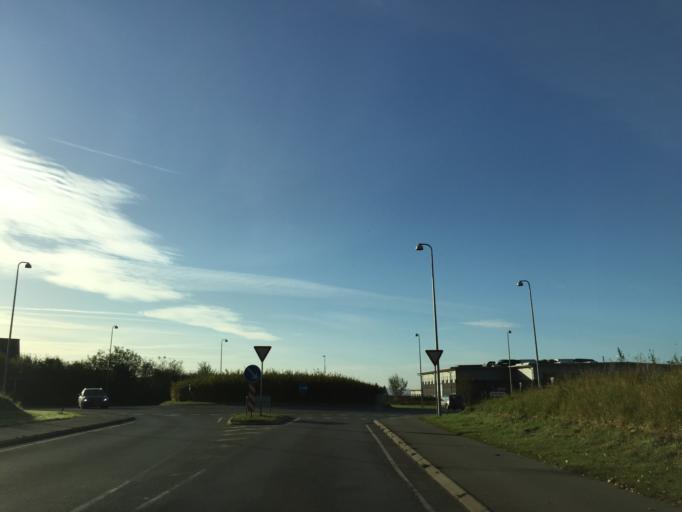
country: DK
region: Central Jutland
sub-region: Skanderborg Kommune
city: Skanderborg
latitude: 56.0481
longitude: 9.9197
